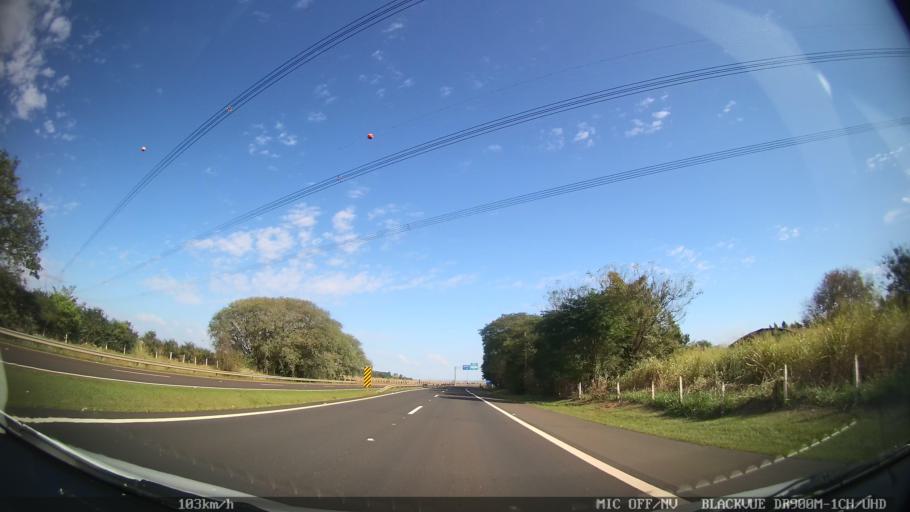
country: BR
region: Sao Paulo
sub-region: Iracemapolis
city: Iracemapolis
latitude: -22.6480
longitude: -47.5122
